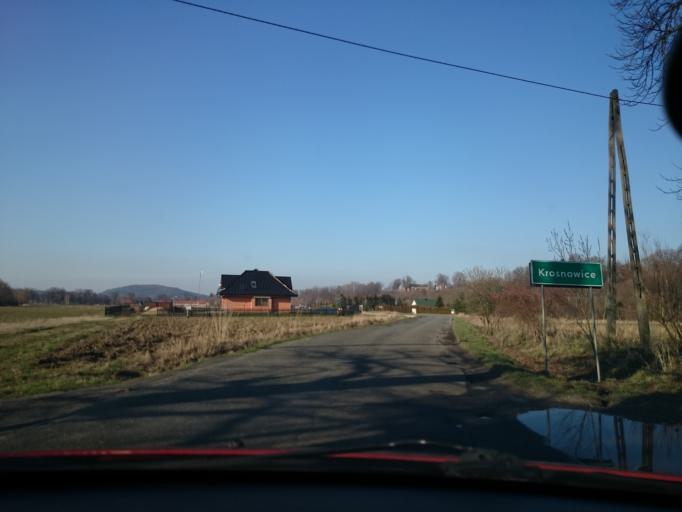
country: PL
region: Lower Silesian Voivodeship
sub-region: Powiat klodzki
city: Klodzko
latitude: 50.3714
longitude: 16.6365
